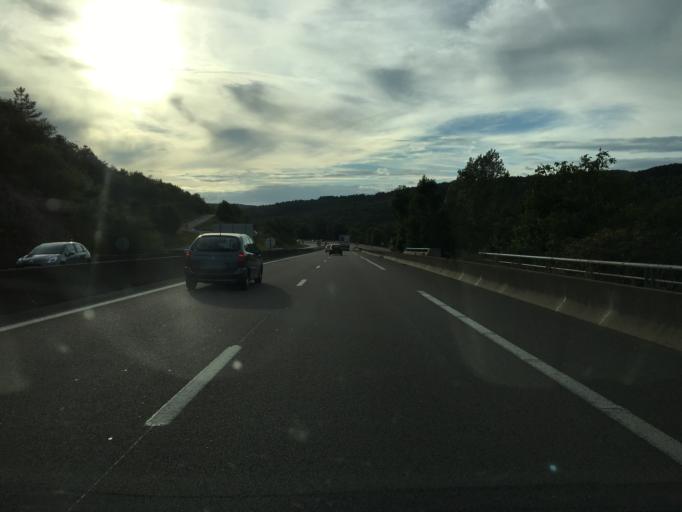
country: FR
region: Bourgogne
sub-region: Departement de la Cote-d'Or
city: Plombieres-les-Dijon
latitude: 47.3370
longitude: 4.9673
